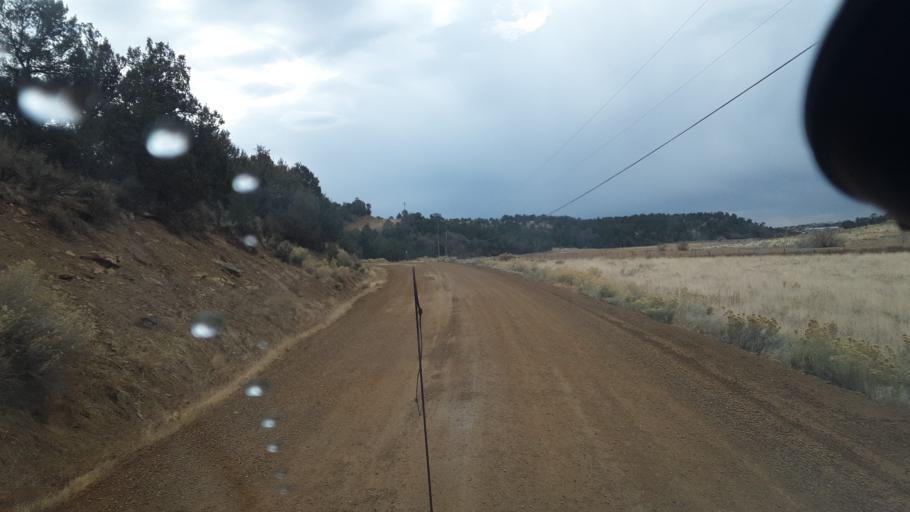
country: US
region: Colorado
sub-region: Montezuma County
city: Mancos
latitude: 37.2025
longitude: -108.1389
